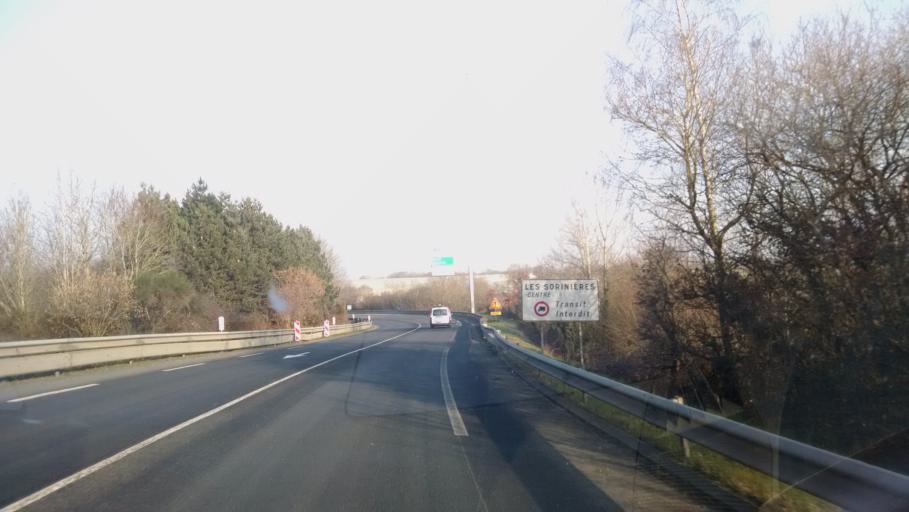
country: FR
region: Pays de la Loire
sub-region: Departement de la Loire-Atlantique
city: Les Sorinieres
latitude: 47.1305
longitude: -1.5046
